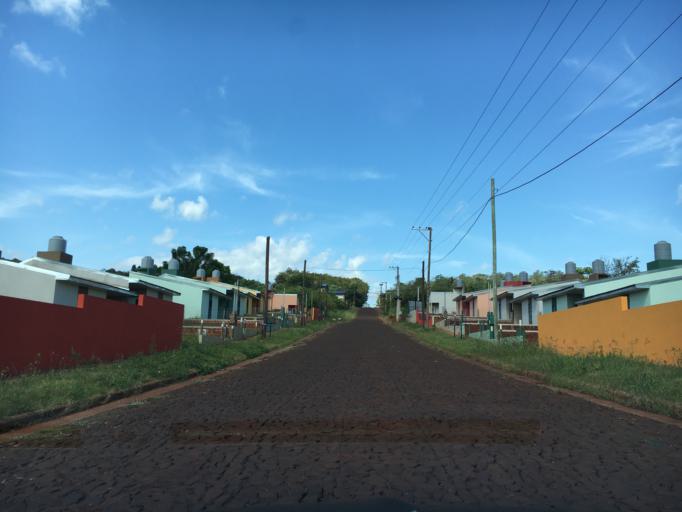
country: AR
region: Misiones
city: Puerto Rico
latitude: -26.8167
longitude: -55.0361
